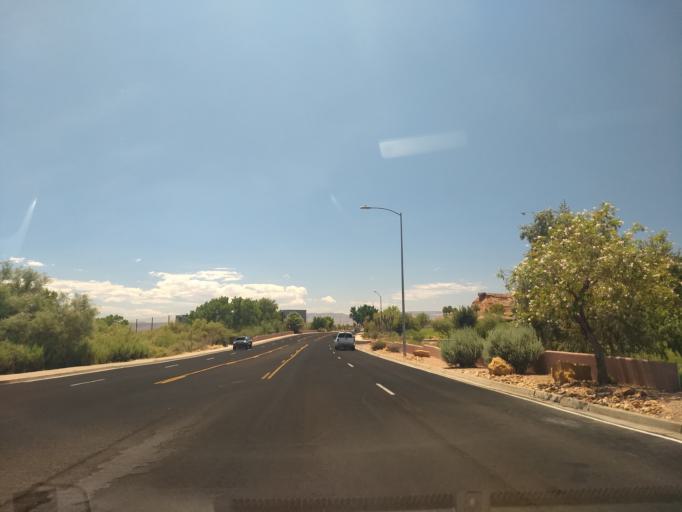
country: US
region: Utah
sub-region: Washington County
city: Washington
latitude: 37.1359
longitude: -113.5263
